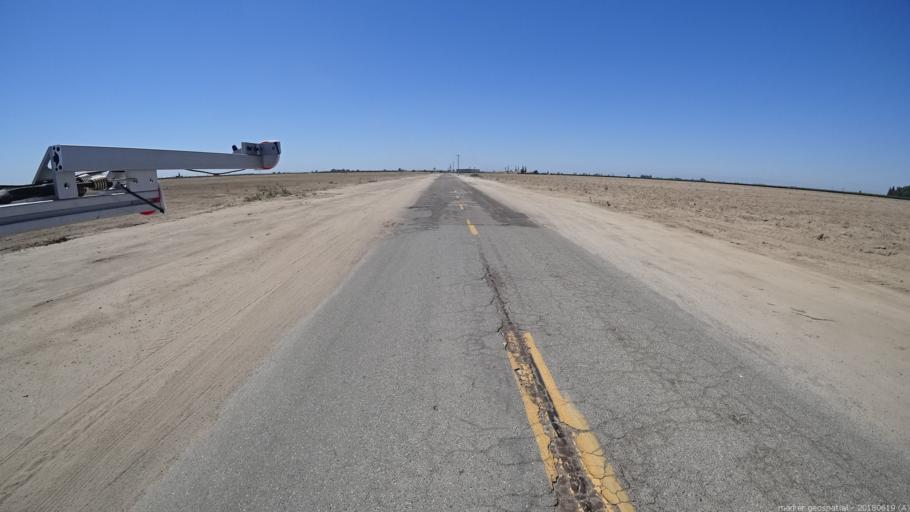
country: US
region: California
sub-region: Fresno County
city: Biola
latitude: 36.8505
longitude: -120.0650
